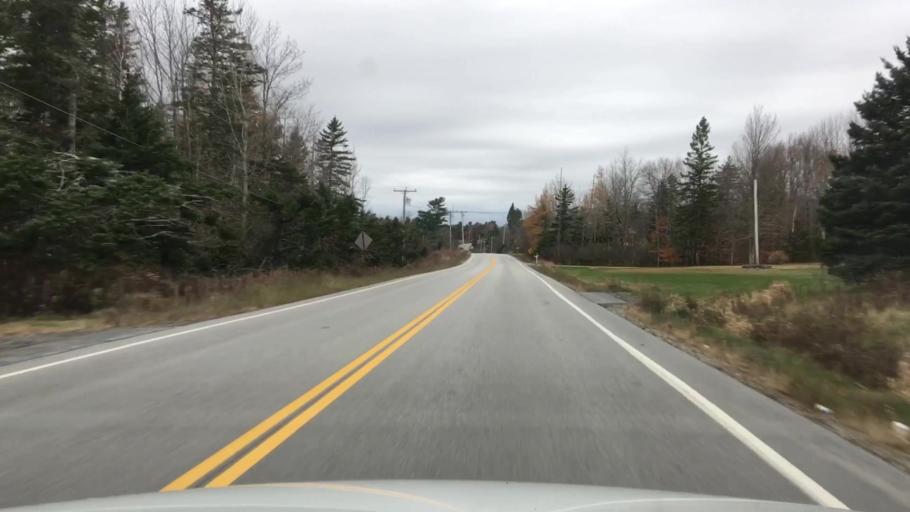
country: US
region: Maine
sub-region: Hancock County
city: Penobscot
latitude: 44.5274
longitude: -68.6672
